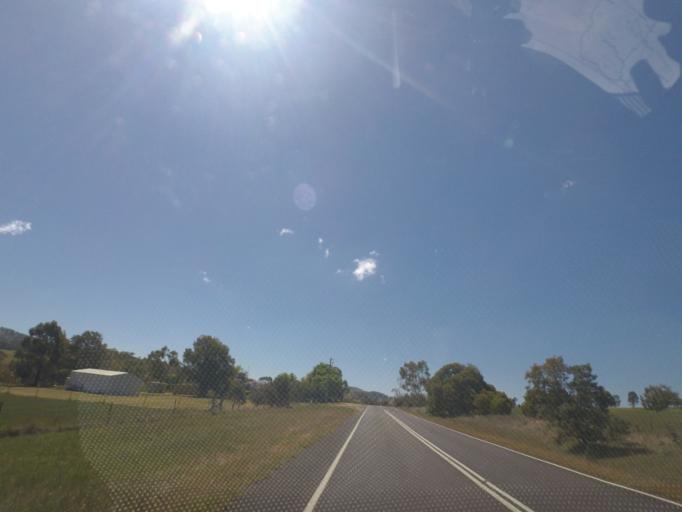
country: AU
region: Victoria
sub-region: Hume
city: Sunbury
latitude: -37.0923
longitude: 144.7596
